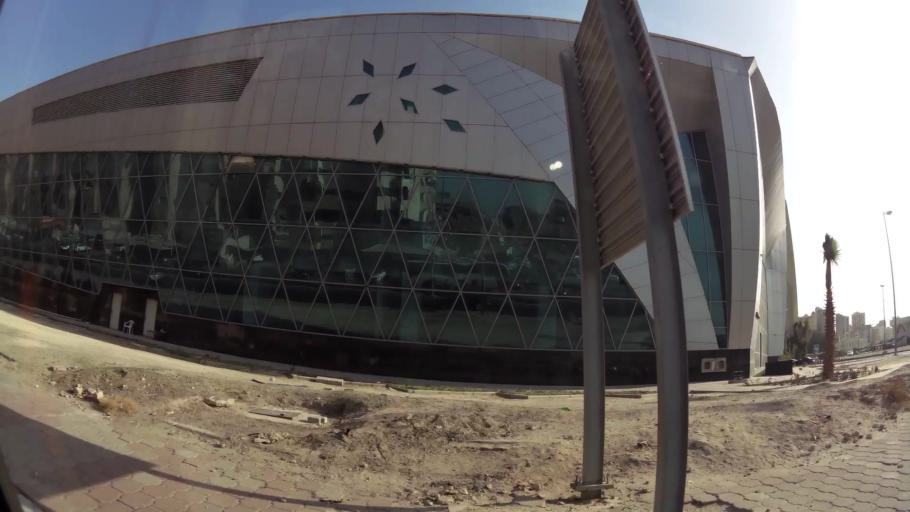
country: KW
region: Muhafazat Hawalli
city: As Salimiyah
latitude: 29.3408
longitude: 48.0843
